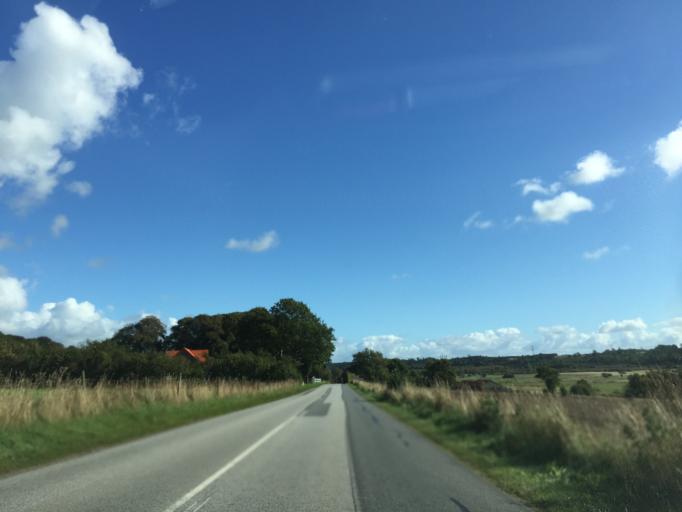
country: DK
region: Central Jutland
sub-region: Viborg Kommune
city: Bjerringbro
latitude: 56.4396
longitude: 9.5421
